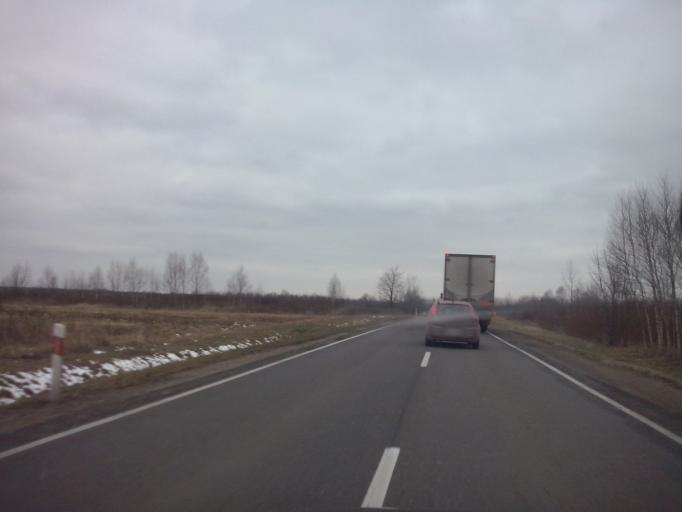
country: PL
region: Subcarpathian Voivodeship
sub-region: Powiat nizanski
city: Przedzel
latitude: 50.4708
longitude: 22.2377
